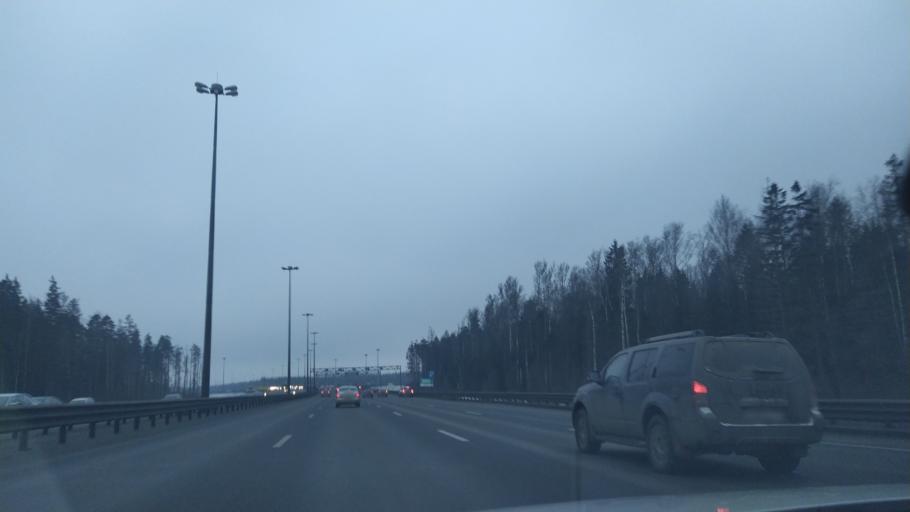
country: RU
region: Leningrad
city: Yanino Vtoroye
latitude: 59.9518
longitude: 30.5457
